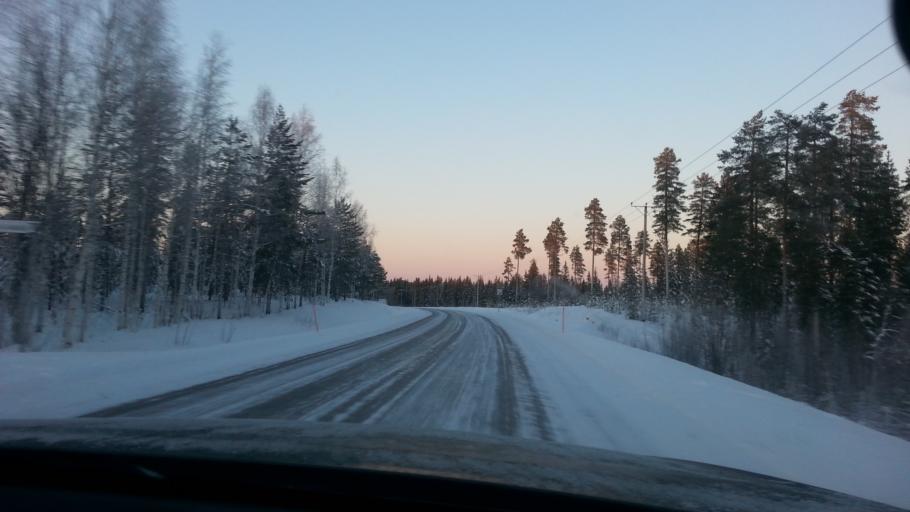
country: FI
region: Lapland
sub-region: Rovaniemi
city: Rovaniemi
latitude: 66.7875
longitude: 25.4420
